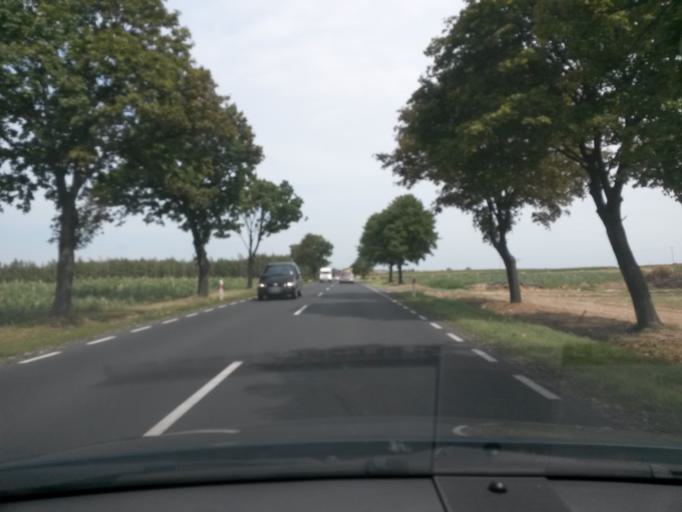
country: PL
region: Greater Poland Voivodeship
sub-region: Powiat sremski
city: Dolsk
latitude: 51.9448
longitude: 17.0423
